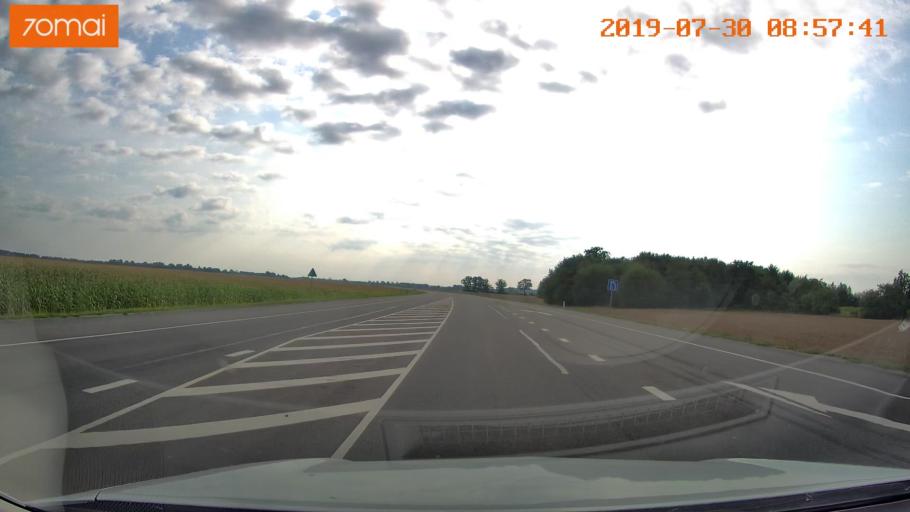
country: RU
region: Kaliningrad
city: Gusev
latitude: 54.6034
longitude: 22.1105
